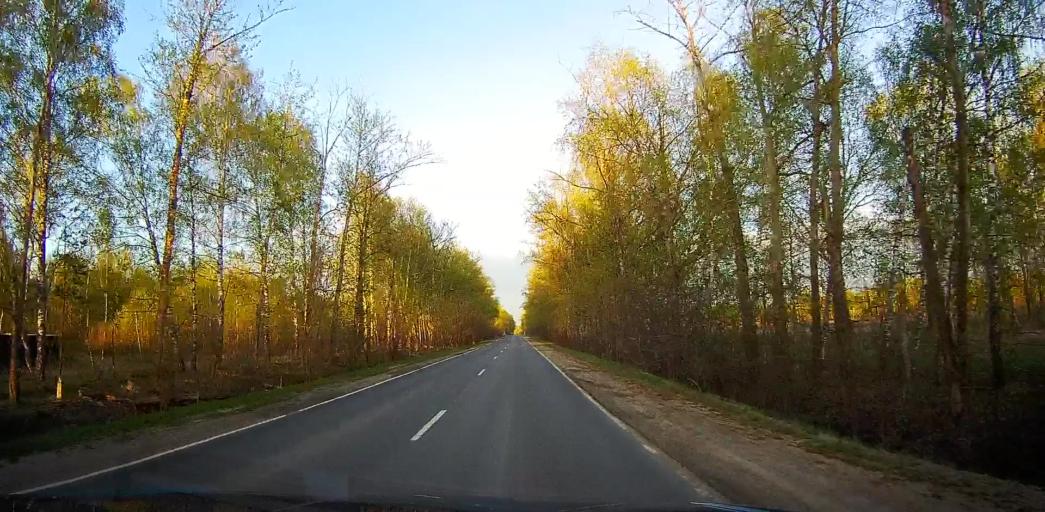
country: RU
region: Moskovskaya
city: Peski
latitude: 55.2089
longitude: 38.7177
